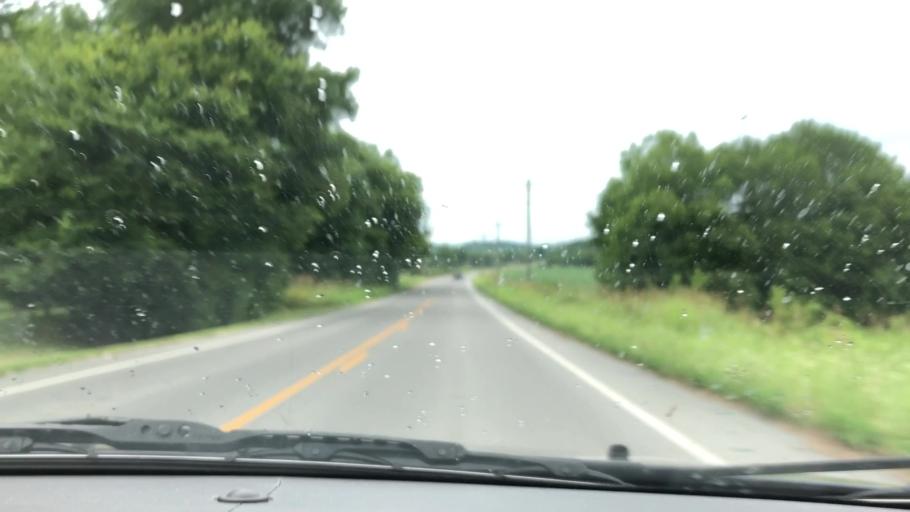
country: US
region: Tennessee
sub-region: Williamson County
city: Thompson's Station
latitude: 35.8327
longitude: -86.9669
